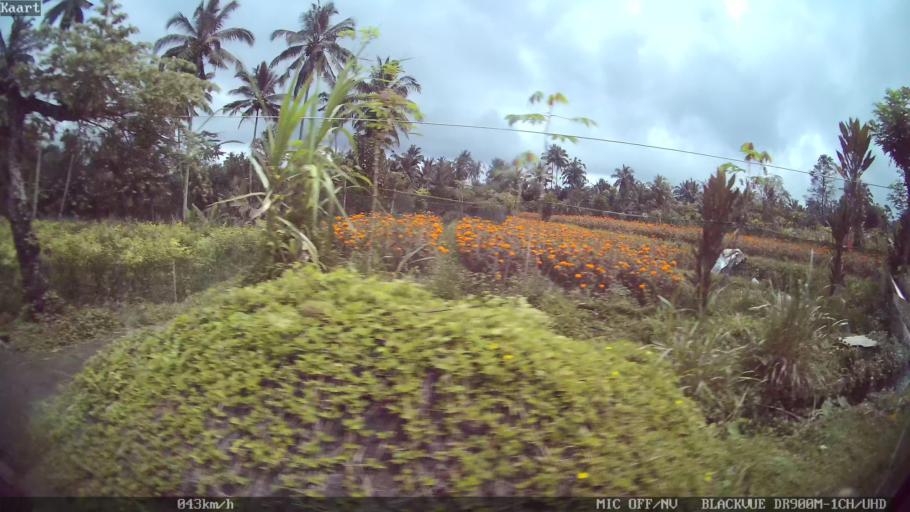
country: ID
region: Bali
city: Banjar Geriana Kangin
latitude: -8.4203
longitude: 115.4362
